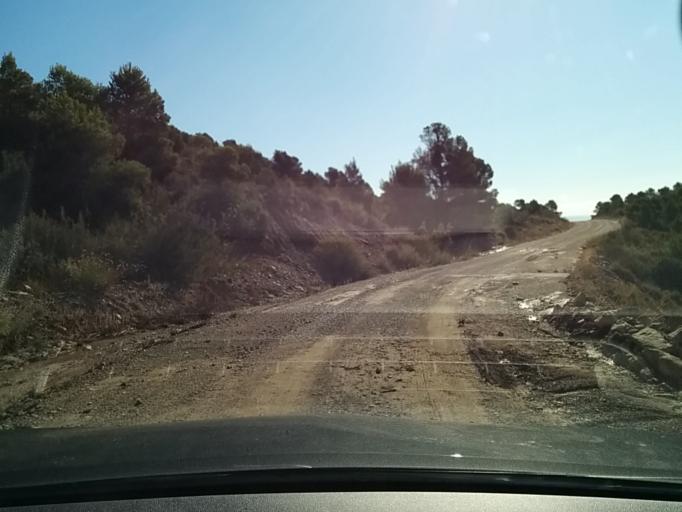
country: ES
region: Aragon
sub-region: Provincia de Zaragoza
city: Novillas
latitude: 42.0193
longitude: -1.3216
